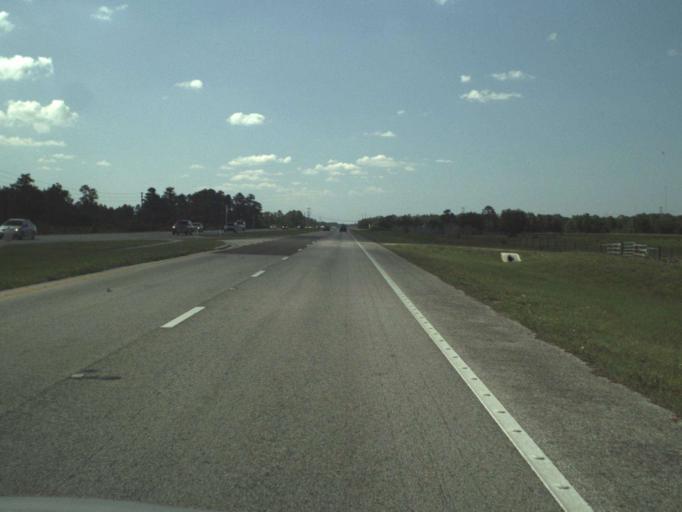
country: US
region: Florida
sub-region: Orange County
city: Wedgefield
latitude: 28.4923
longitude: -81.0424
